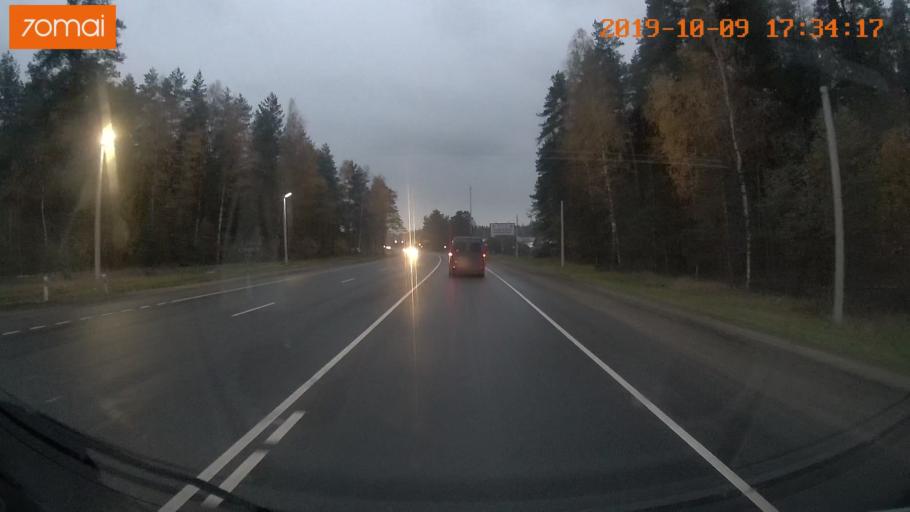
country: RU
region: Ivanovo
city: Bogorodskoye
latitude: 57.1080
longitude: 41.0129
